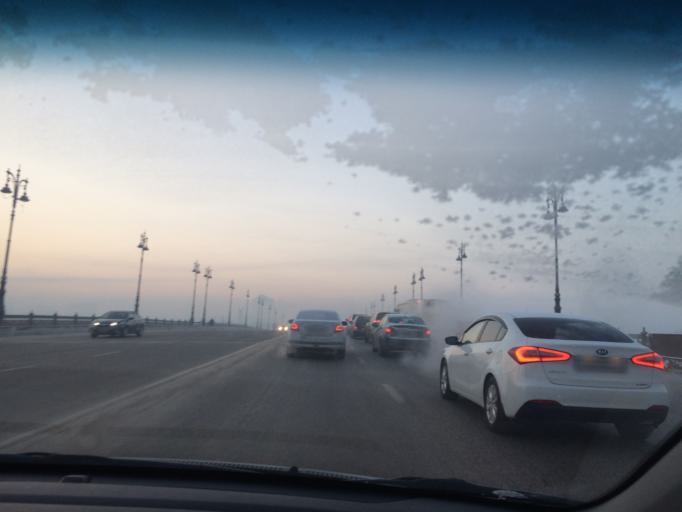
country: KZ
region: Astana Qalasy
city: Astana
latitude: 51.1589
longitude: 71.4110
